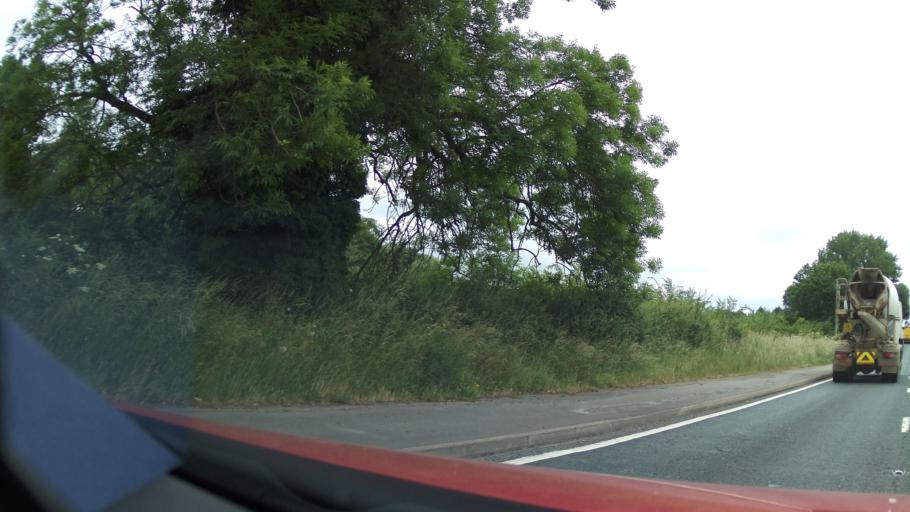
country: GB
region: England
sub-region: Leicestershire
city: Kirby Muxloe
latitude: 52.6661
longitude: -1.2377
